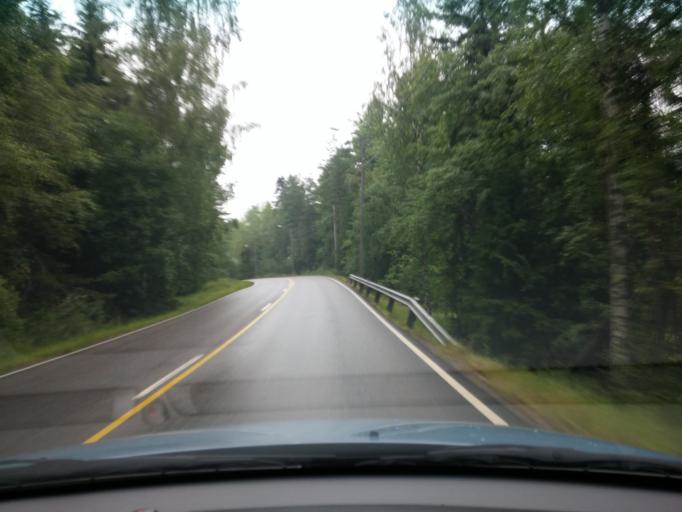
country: FI
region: Uusimaa
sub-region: Helsinki
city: Nurmijaervi
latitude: 60.3516
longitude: 24.7430
